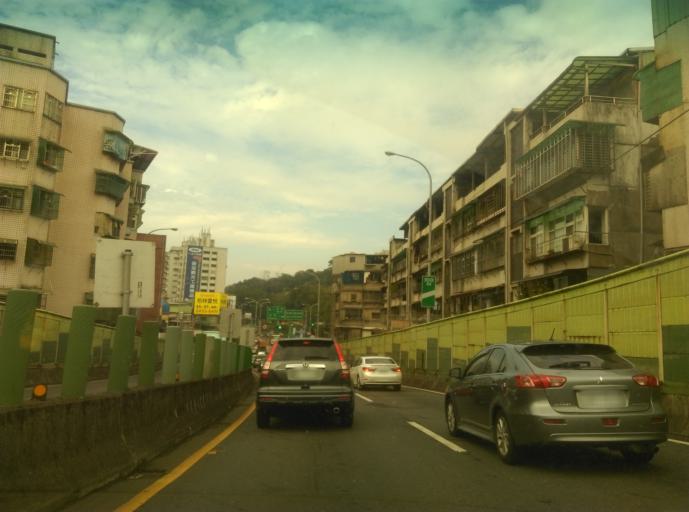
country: TW
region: Taiwan
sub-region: Keelung
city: Keelung
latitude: 25.1409
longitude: 121.7036
